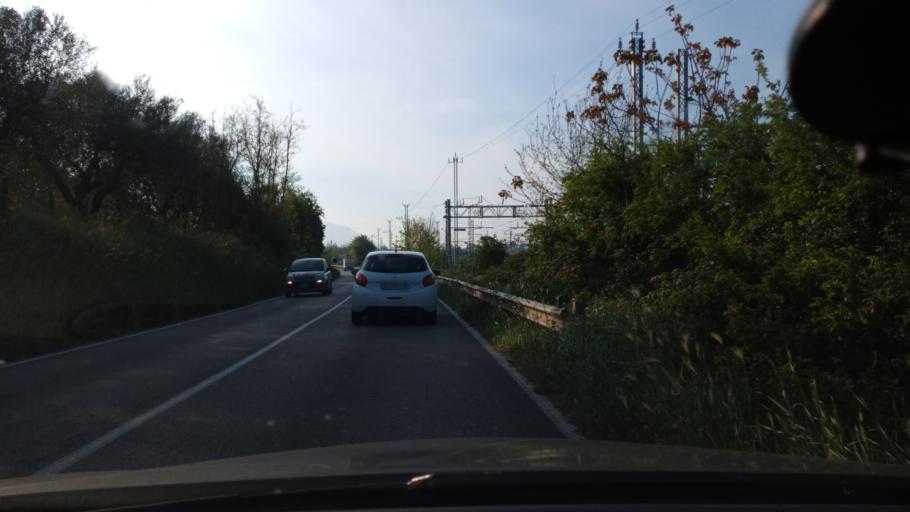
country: IT
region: Latium
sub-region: Citta metropolitana di Roma Capitale
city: Fiano Romano
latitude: 42.1651
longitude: 12.6432
